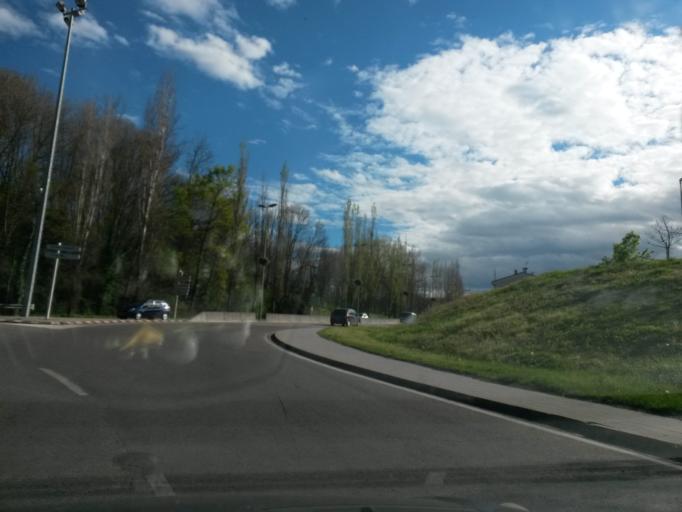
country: ES
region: Catalonia
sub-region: Provincia de Girona
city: Olot
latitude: 42.1667
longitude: 2.4736
